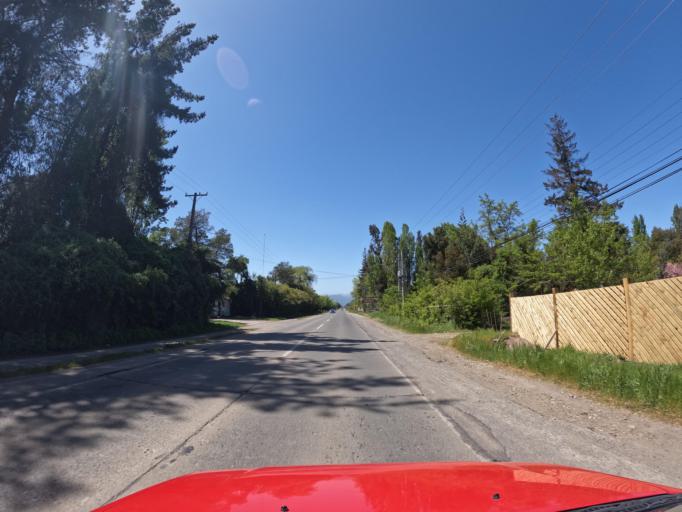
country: CL
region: Maule
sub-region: Provincia de Linares
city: Linares
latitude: -35.8339
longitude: -71.5407
